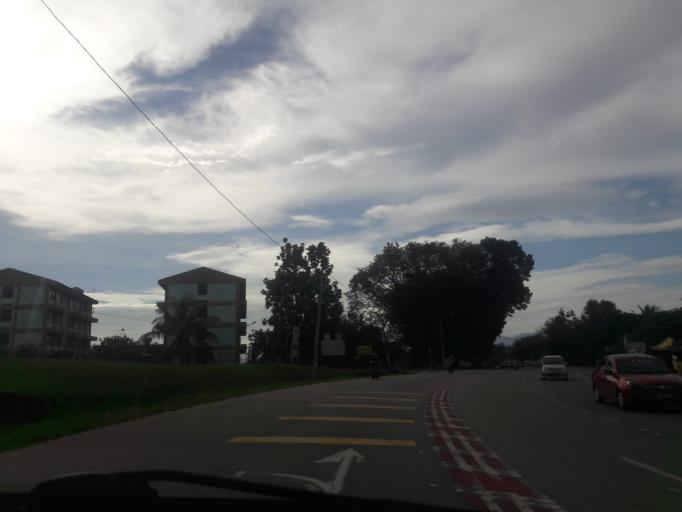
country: MY
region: Kedah
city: Sungai Petani
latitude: 5.6283
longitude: 100.5255
